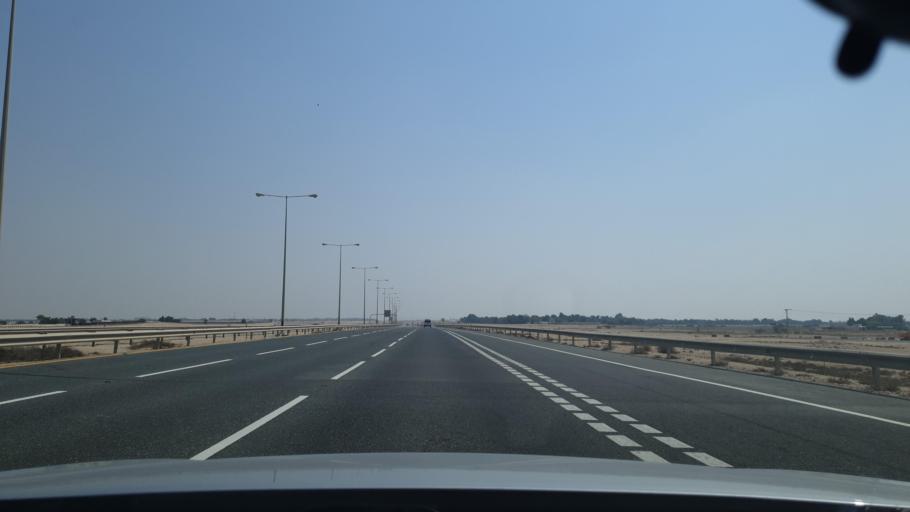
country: QA
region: Al Khawr
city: Al Khawr
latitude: 25.7862
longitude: 51.3962
